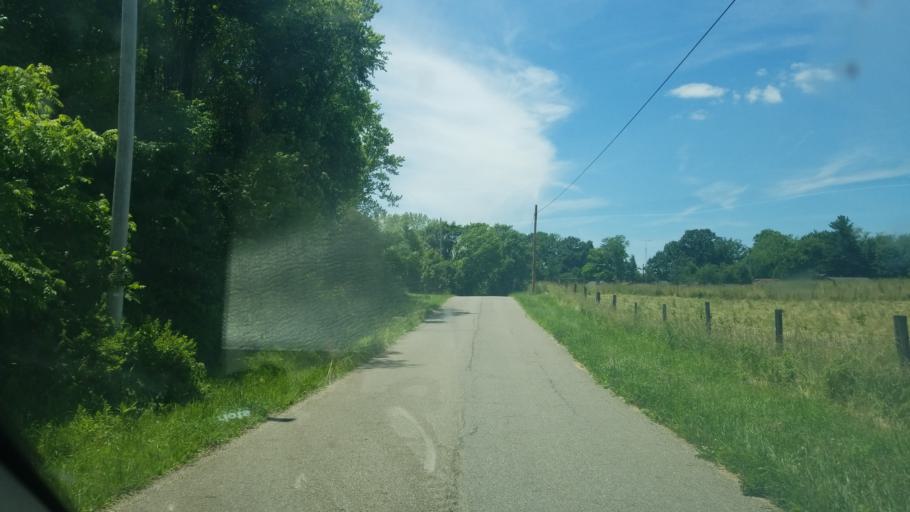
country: US
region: Ohio
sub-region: Mahoning County
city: Sebring
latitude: 40.8504
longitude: -80.9882
